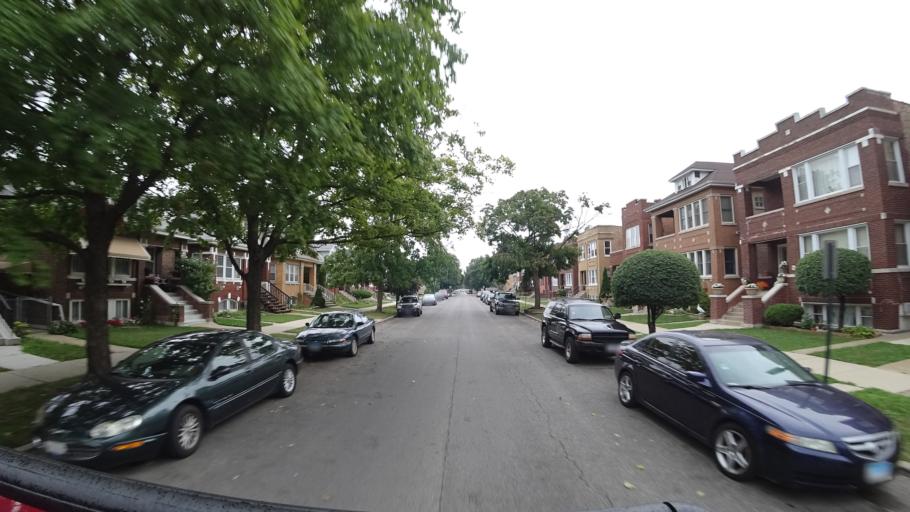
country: US
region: Illinois
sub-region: Cook County
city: Cicero
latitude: 41.8537
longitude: -87.7529
